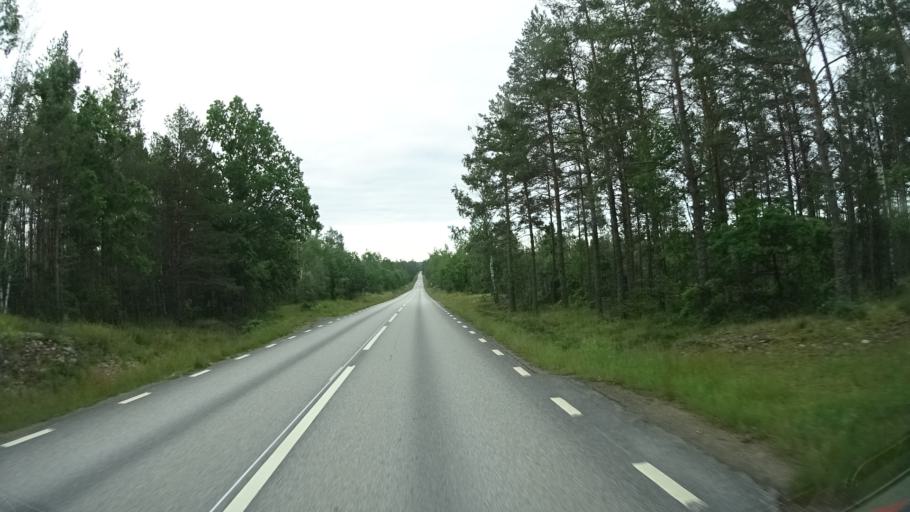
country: SE
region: Kalmar
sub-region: Oskarshamns Kommun
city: Oskarshamn
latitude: 57.2746
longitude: 16.3051
